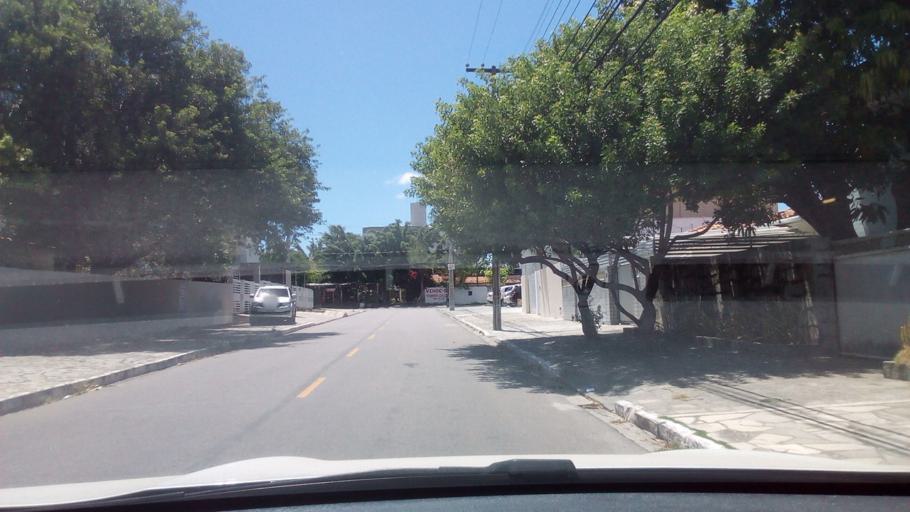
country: BR
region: Paraiba
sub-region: Joao Pessoa
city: Joao Pessoa
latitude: -7.1499
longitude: -34.8380
